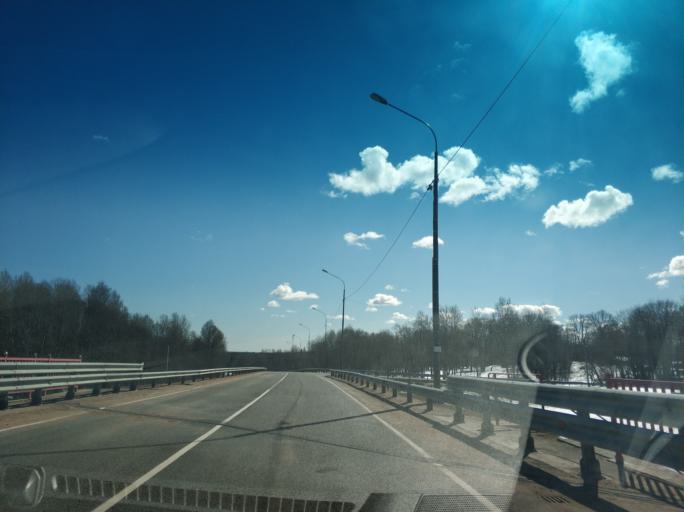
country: RU
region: Leningrad
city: Sosnovo
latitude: 60.4332
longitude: 30.2364
